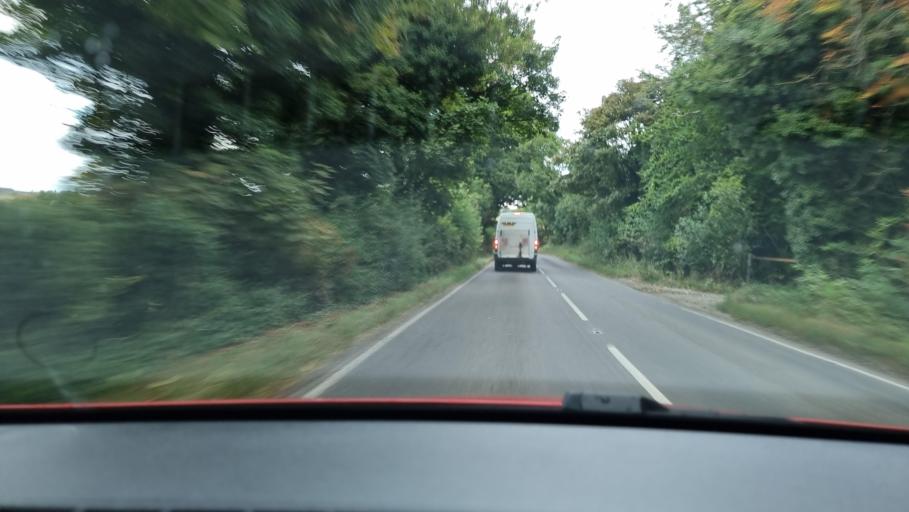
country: GB
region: England
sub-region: Buckinghamshire
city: Ivinghoe
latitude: 51.8288
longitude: -0.6238
